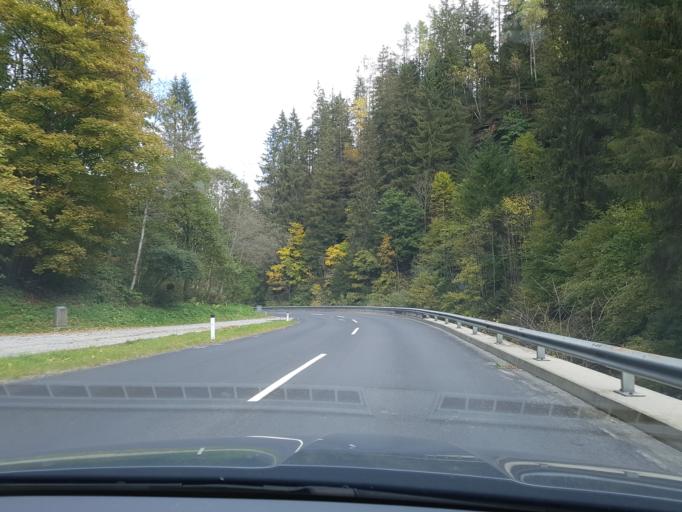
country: AT
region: Styria
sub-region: Politischer Bezirk Murau
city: Stadl an der Mur
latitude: 47.0501
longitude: 13.9080
